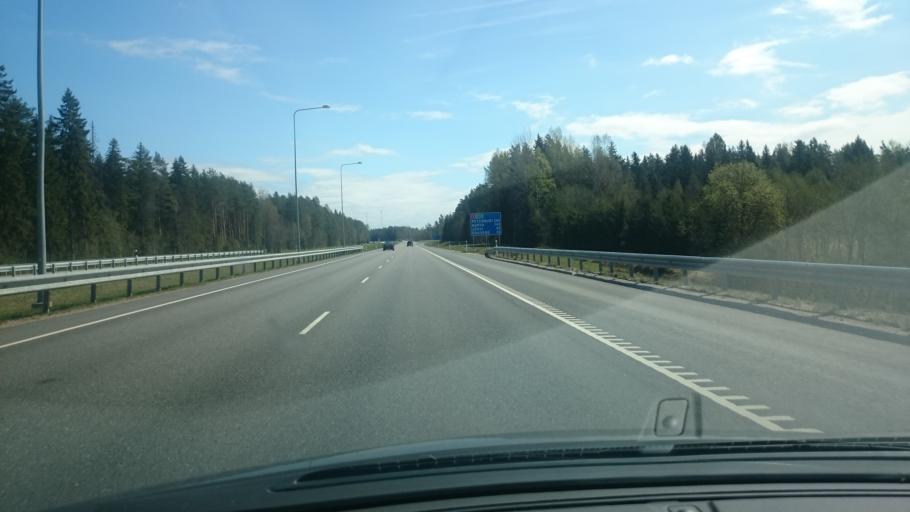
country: EE
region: Laeaene-Virumaa
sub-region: Tapa vald
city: Tapa
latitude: 59.4554
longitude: 25.9505
